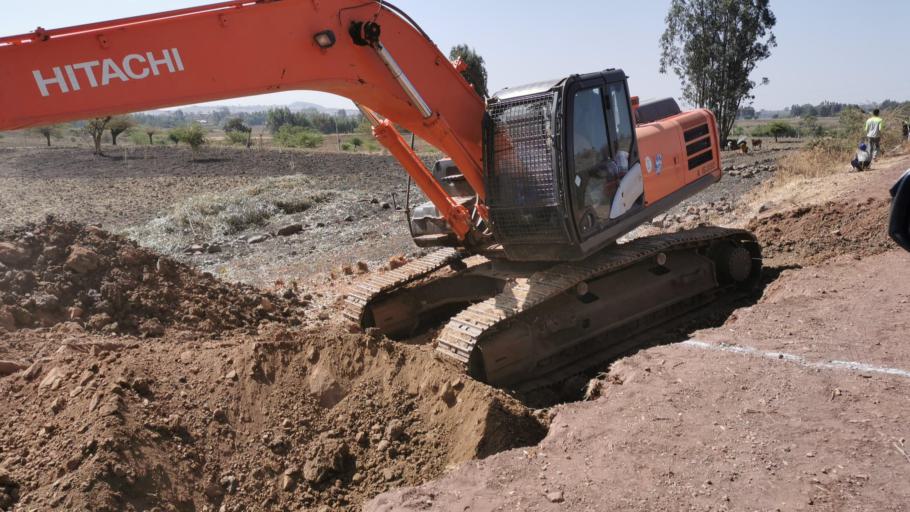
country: ET
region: Amhara
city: Bahir Dar
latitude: 11.8350
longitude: 37.0000
